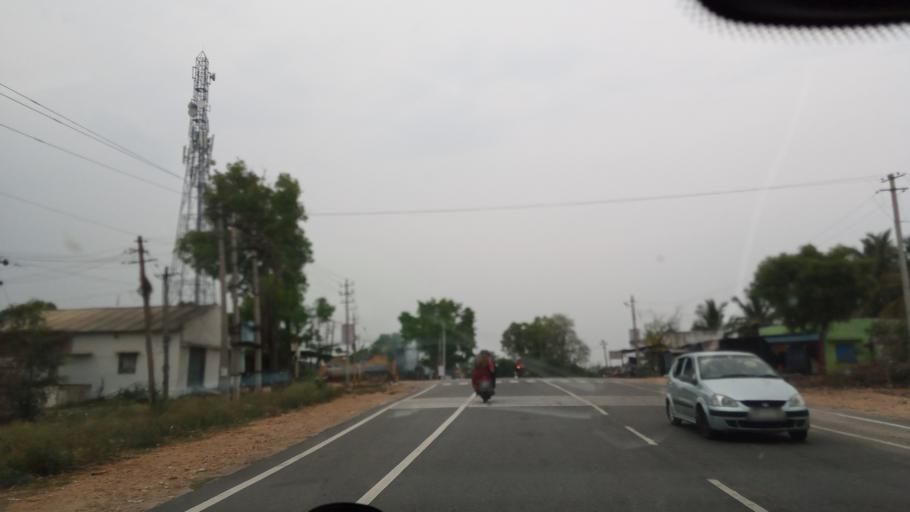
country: IN
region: Karnataka
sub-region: Mandya
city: Belluru
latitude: 12.9449
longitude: 76.7516
